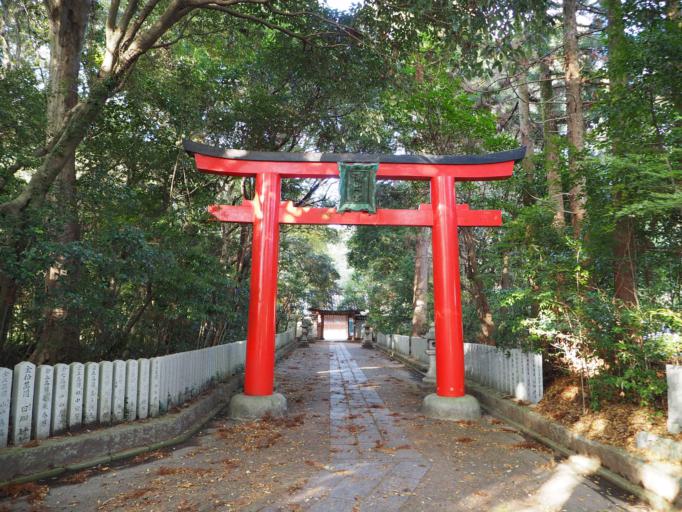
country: JP
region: Kyoto
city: Tanabe
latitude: 34.7746
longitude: 135.8173
